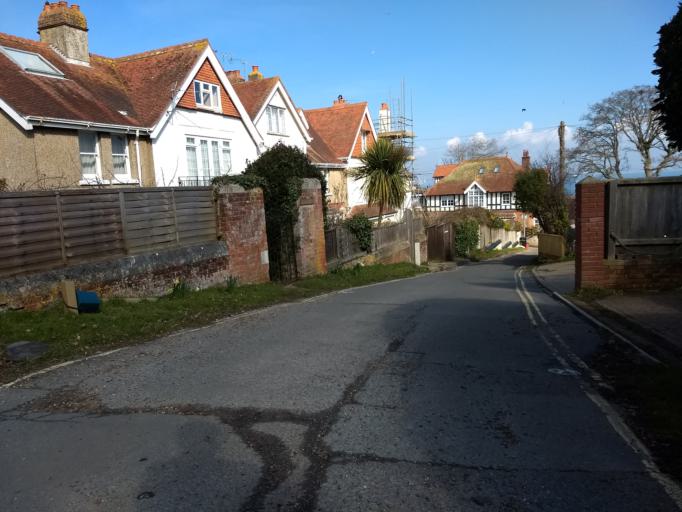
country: GB
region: England
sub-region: Isle of Wight
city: Seaview
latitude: 50.7131
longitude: -1.1070
